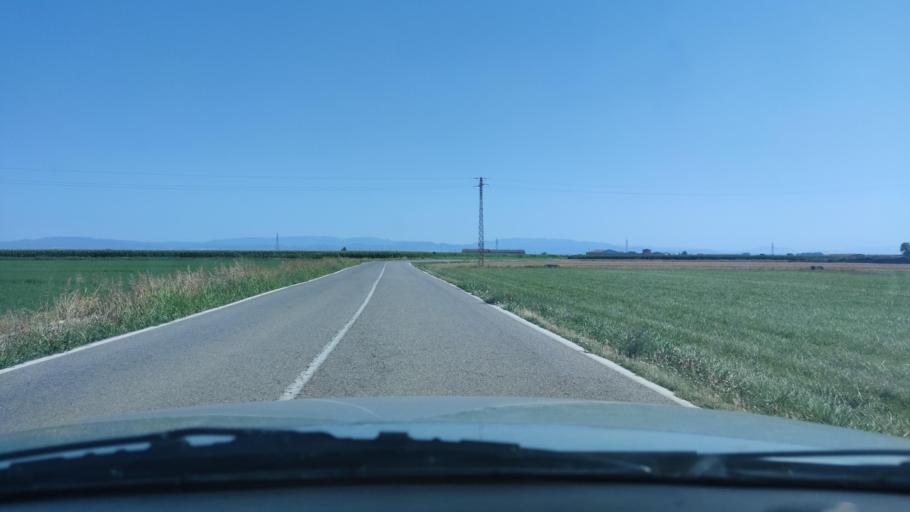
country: ES
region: Catalonia
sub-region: Provincia de Lleida
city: Bellvis
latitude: 41.6418
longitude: 0.7947
